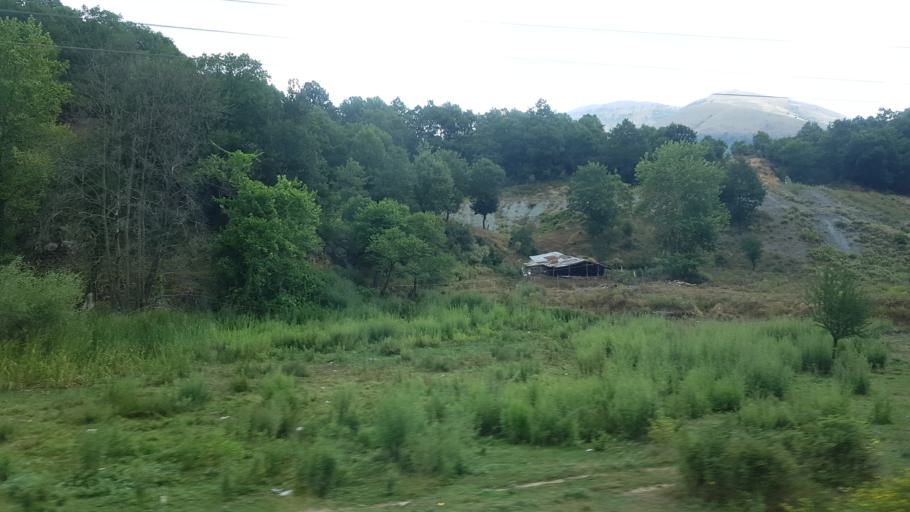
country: AL
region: Vlore
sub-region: Rrethi i Sarandes
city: Dhiver
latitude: 39.9143
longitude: 20.1833
